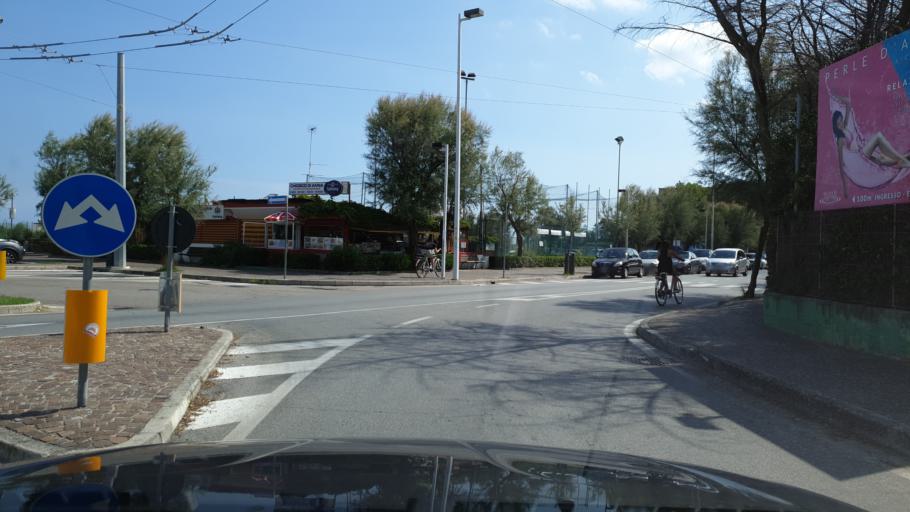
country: IT
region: Emilia-Romagna
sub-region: Provincia di Rimini
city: Riccione
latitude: 43.9953
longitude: 12.6721
